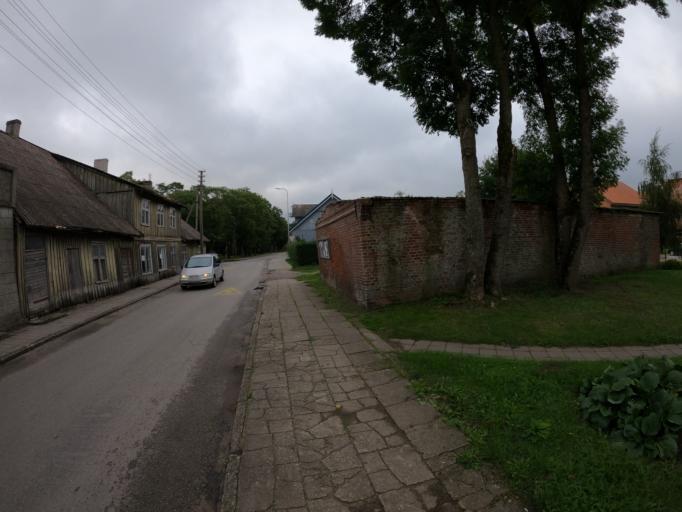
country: LT
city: Rusne
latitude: 55.2974
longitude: 21.3735
